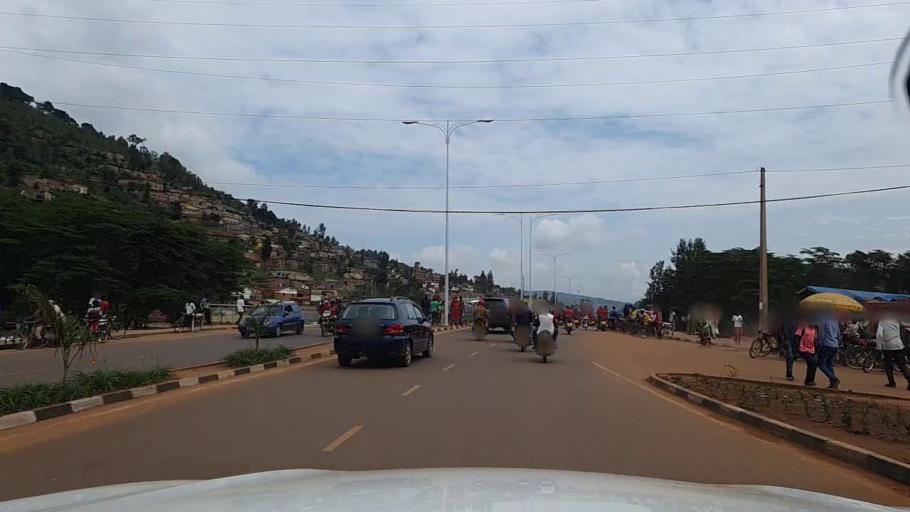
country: RW
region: Kigali
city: Kigali
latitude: -1.9400
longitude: 30.0438
